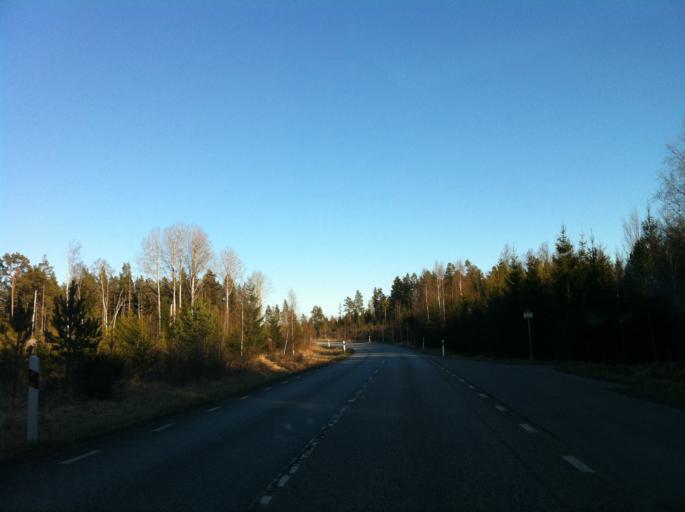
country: SE
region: Uppsala
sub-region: Osthammars Kommun
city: Anneberg
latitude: 60.1679
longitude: 18.4115
